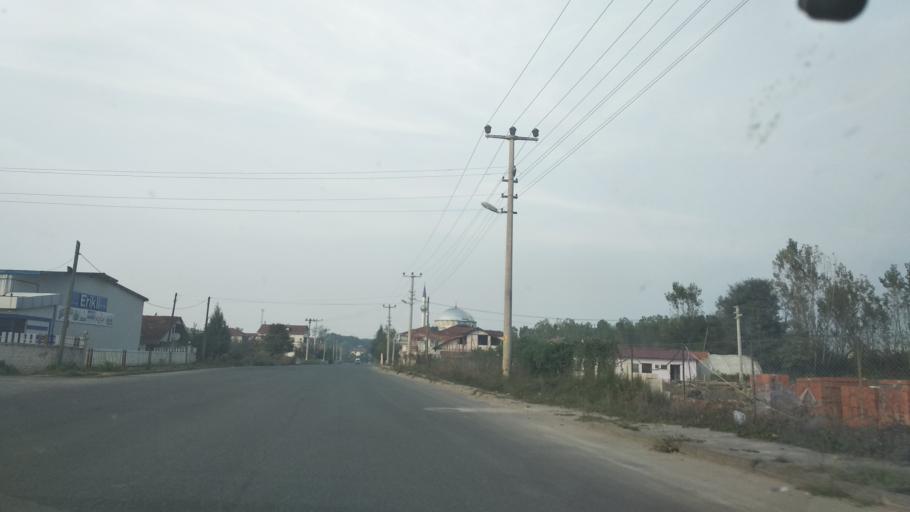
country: TR
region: Duzce
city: Duzce
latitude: 40.8129
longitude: 31.1773
